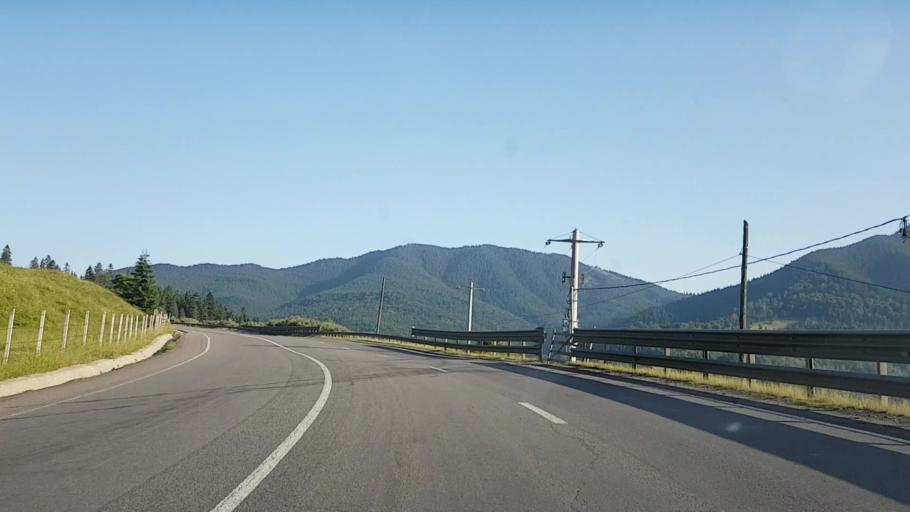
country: RO
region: Bistrita-Nasaud
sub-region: Comuna Lunca Ilvei
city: Lunca Ilvei
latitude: 47.2303
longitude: 24.9666
